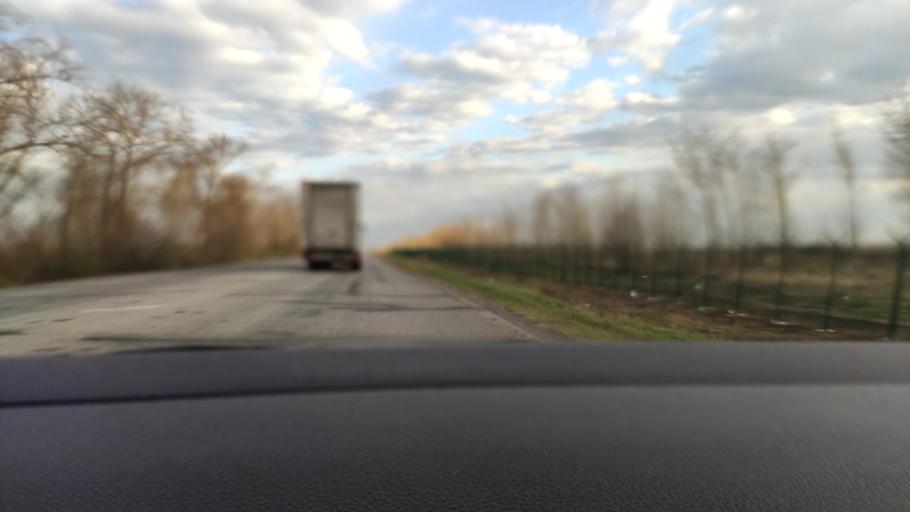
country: RU
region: Voronezj
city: Maslovka
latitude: 51.5367
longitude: 39.2894
